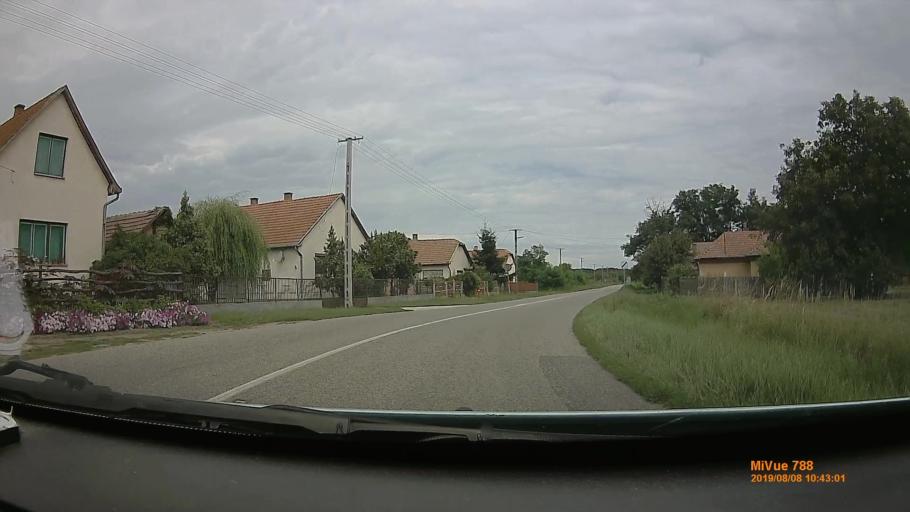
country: HU
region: Hajdu-Bihar
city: Nyiradony
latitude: 47.7184
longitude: 21.8773
